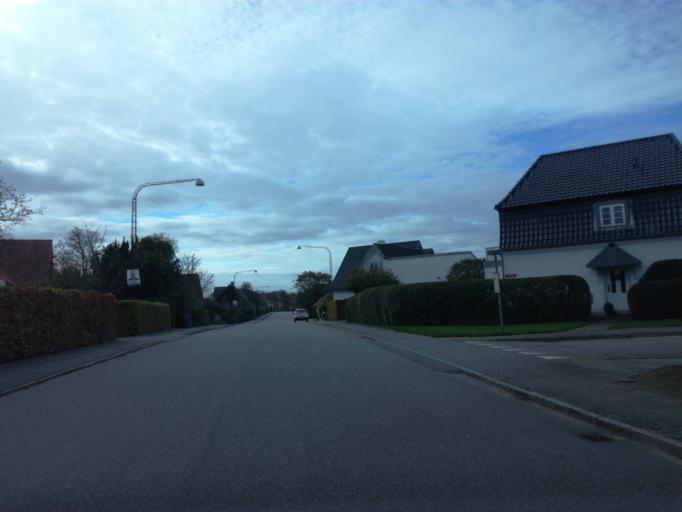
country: DK
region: South Denmark
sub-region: Fredericia Kommune
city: Fredericia
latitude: 55.5758
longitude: 9.7749
